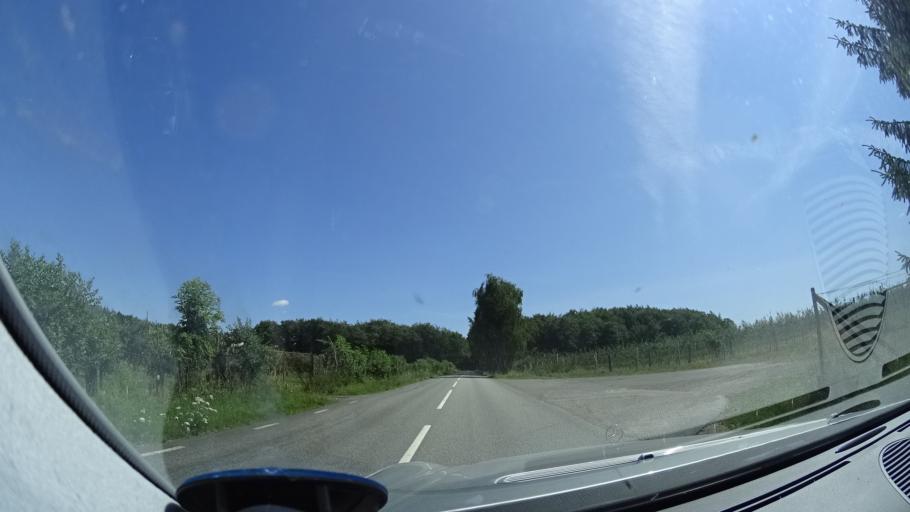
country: SE
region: Skane
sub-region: Kristianstads Kommun
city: Degeberga
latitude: 55.8913
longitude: 14.0056
